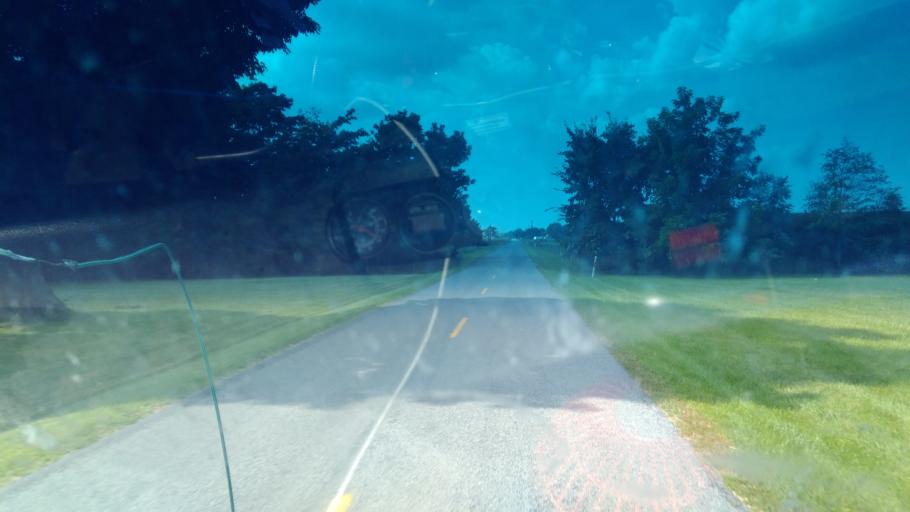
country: US
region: Ohio
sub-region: Hardin County
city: Ada
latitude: 40.7029
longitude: -83.9079
